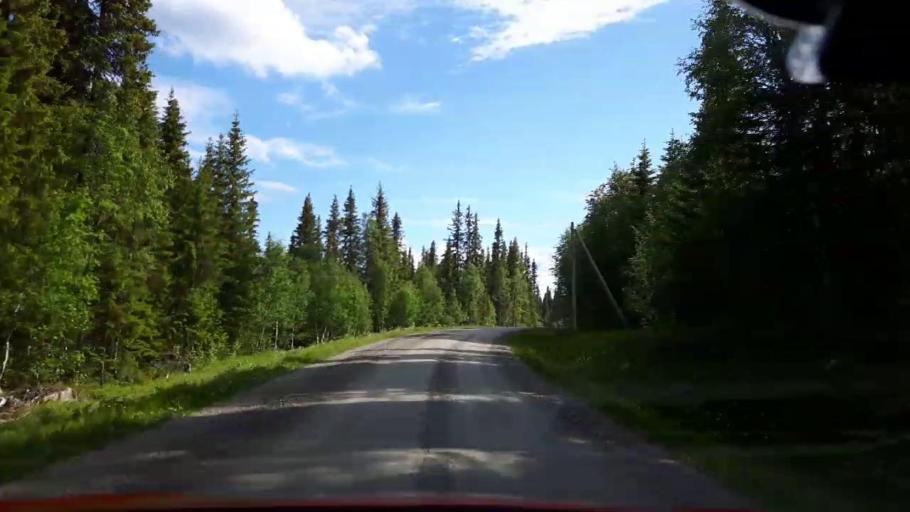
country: SE
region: Jaemtland
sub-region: Krokoms Kommun
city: Valla
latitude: 63.8076
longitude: 14.0499
